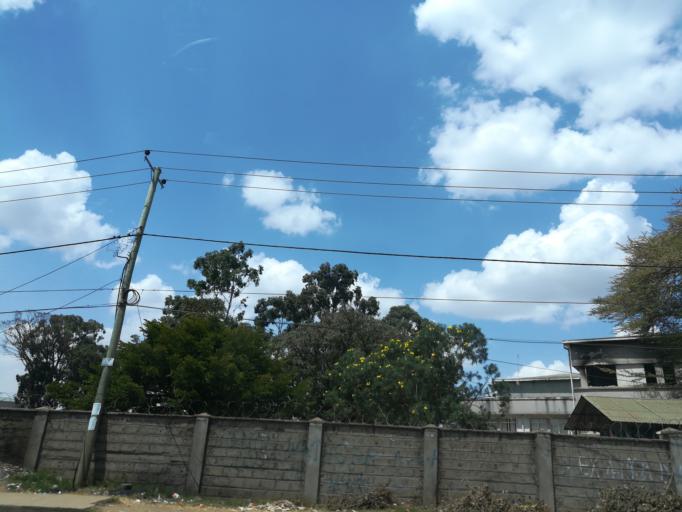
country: KE
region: Nairobi Area
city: Nairobi
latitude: -1.3167
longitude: 36.8133
